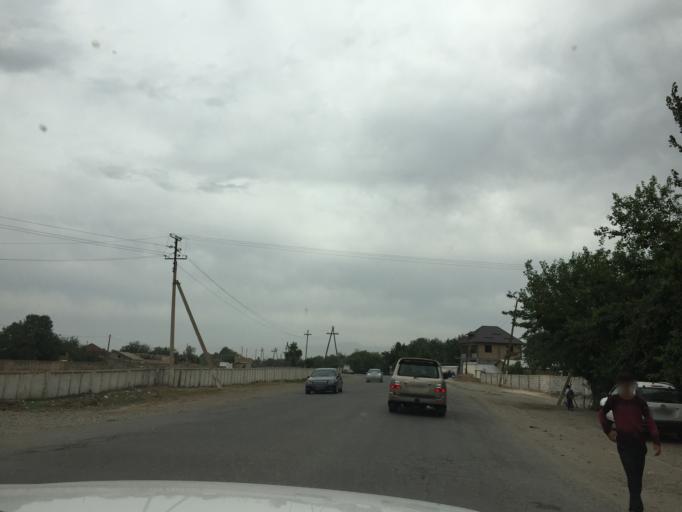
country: TJ
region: Khatlon
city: Moskva
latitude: 37.7436
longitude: 69.4994
